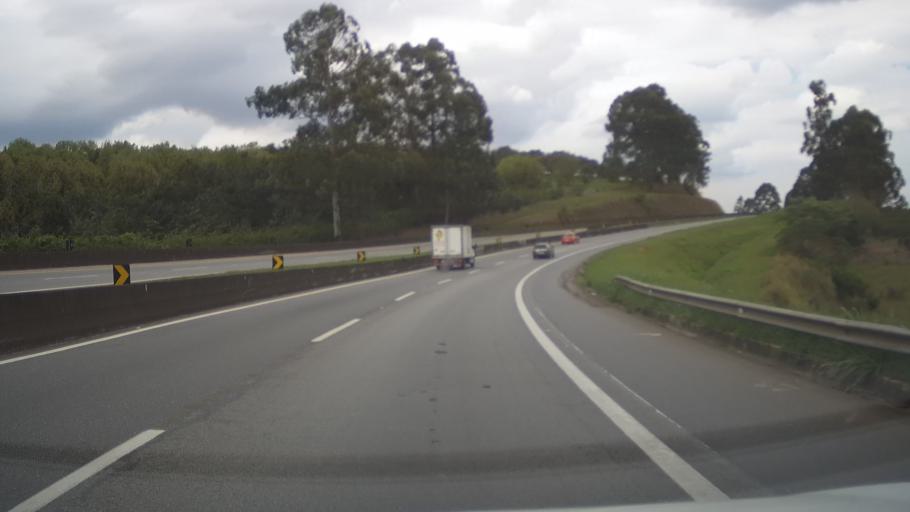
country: BR
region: Minas Gerais
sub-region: Tres Coracoes
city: Tres Coracoes
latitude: -21.5012
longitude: -45.2147
